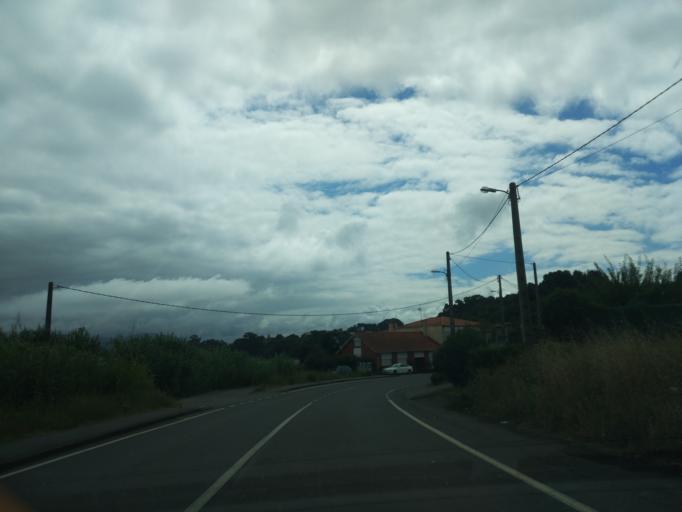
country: ES
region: Galicia
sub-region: Provincia da Coruna
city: Boiro
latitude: 42.6432
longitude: -8.8602
